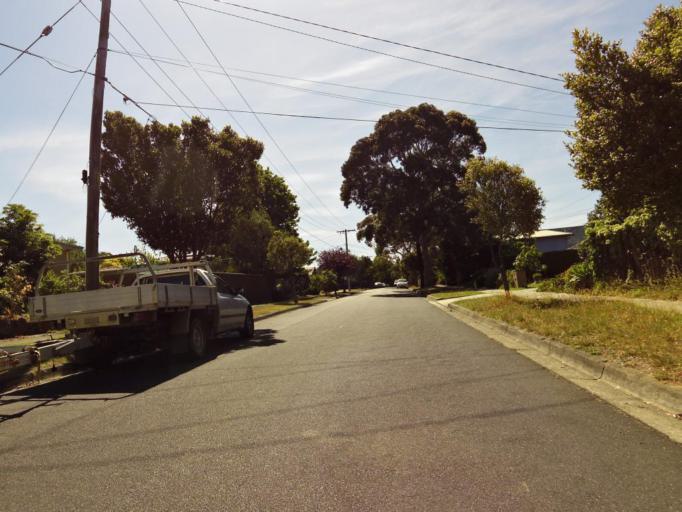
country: AU
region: Victoria
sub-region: Monash
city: Mulgrave
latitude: -37.8966
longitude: 145.1765
